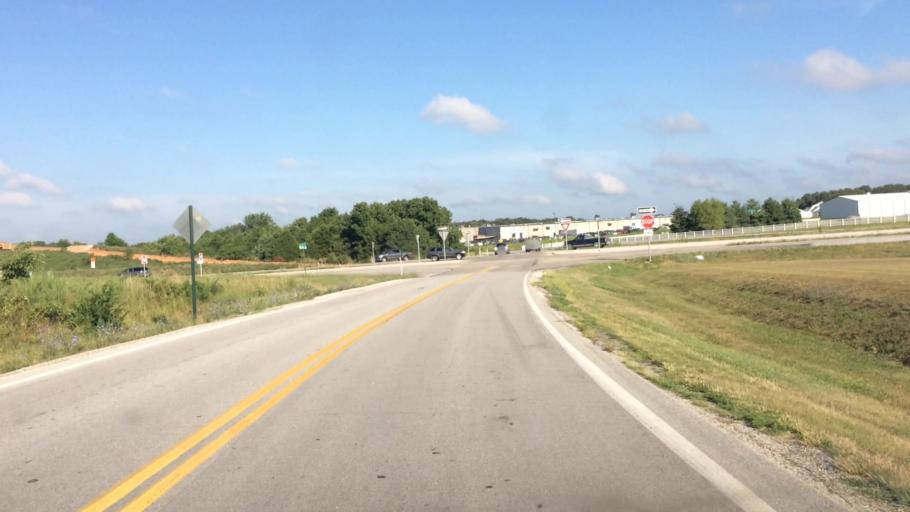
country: US
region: Missouri
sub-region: Greene County
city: Strafford
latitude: 37.2725
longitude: -93.2136
